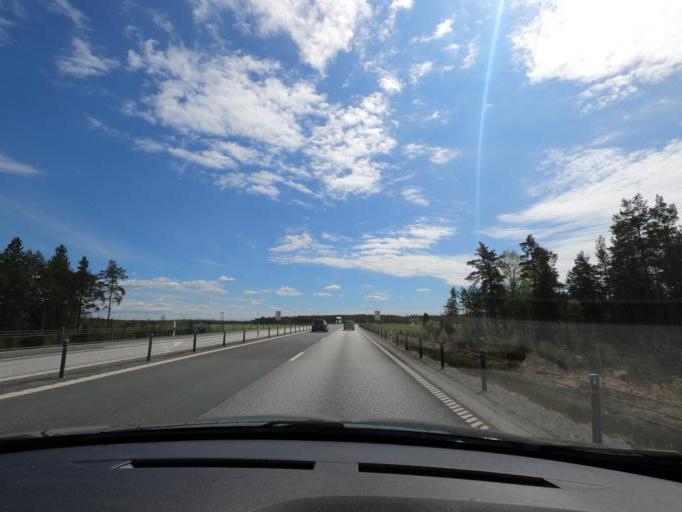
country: SE
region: Joenkoeping
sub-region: Gislaveds Kommun
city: Gislaved
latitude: 57.3165
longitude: 13.5631
